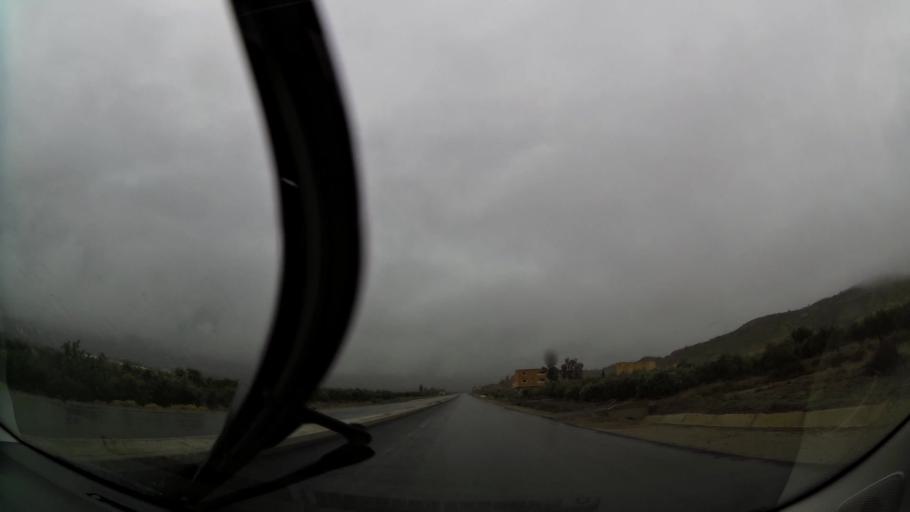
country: MA
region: Oriental
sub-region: Nador
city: Midar
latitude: 34.8361
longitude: -3.7202
